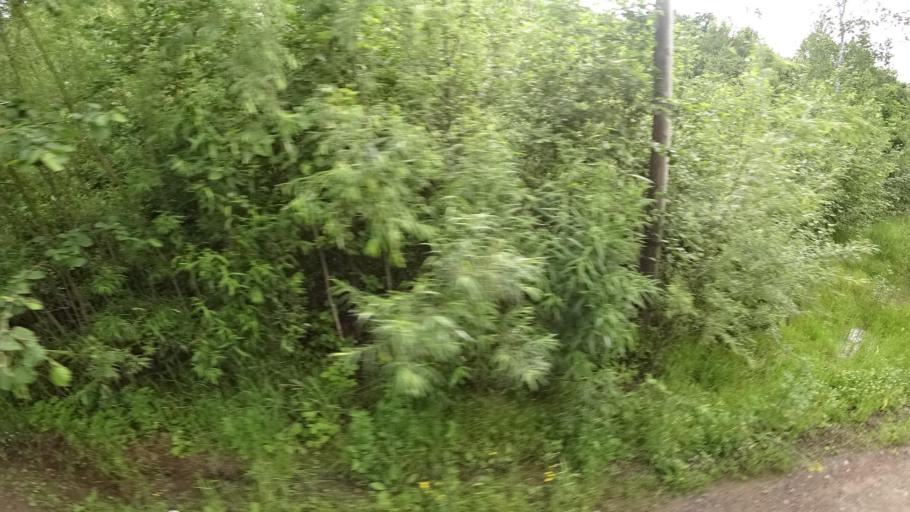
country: RU
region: Khabarovsk Krai
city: Litovko
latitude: 49.3619
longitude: 135.1797
